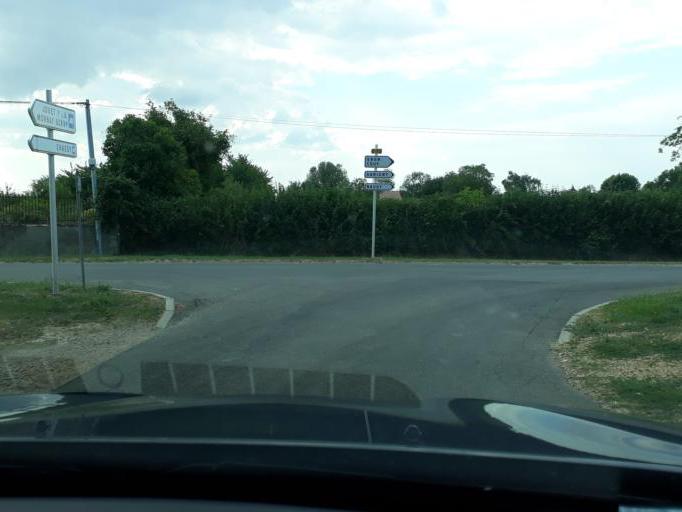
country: FR
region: Centre
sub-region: Departement du Cher
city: Nerondes
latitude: 47.0675
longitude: 2.8031
